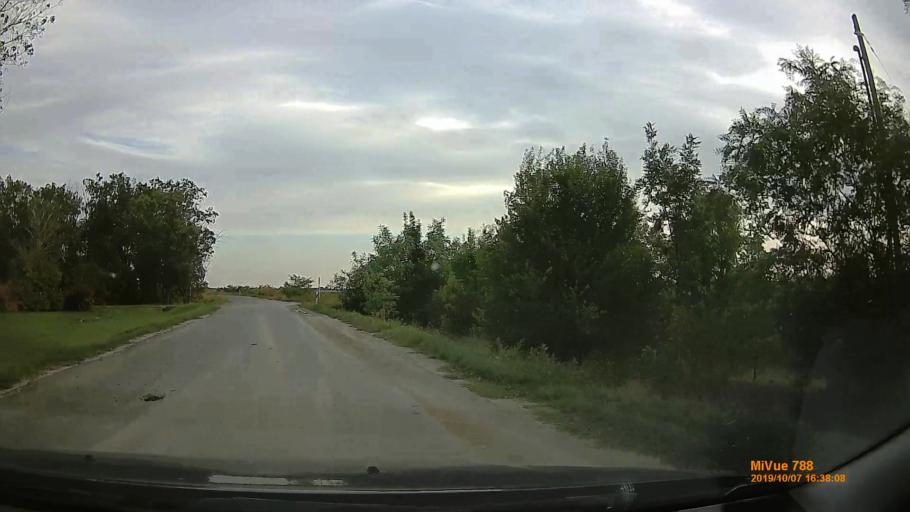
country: HU
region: Bekes
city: Szarvas
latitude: 46.8153
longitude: 20.6070
